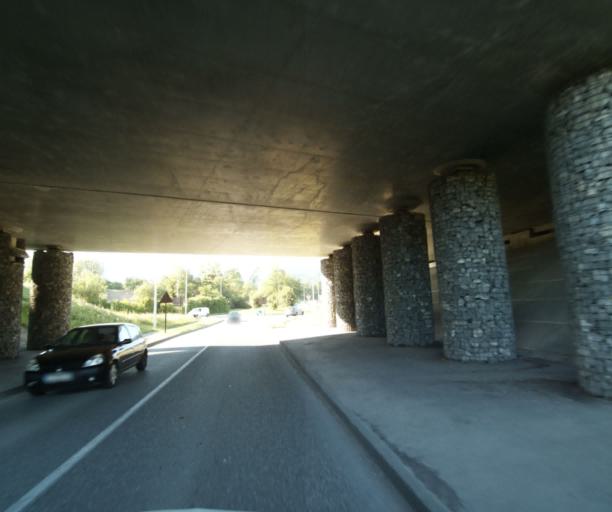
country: FR
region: Rhone-Alpes
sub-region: Departement de la Haute-Savoie
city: Allinges
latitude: 46.3522
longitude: 6.4590
